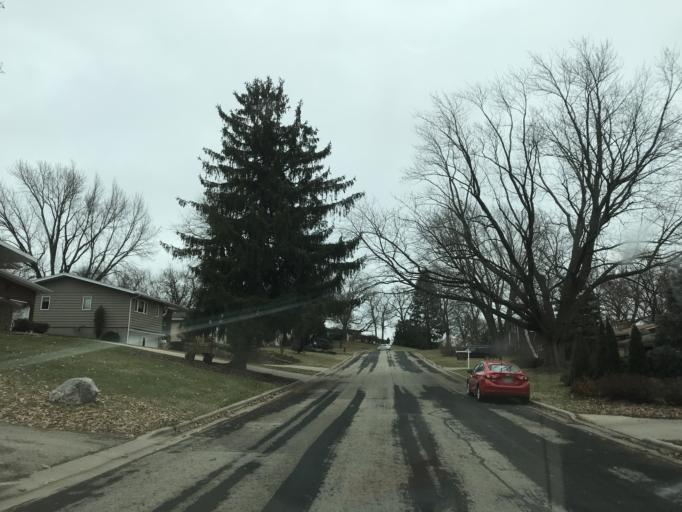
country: US
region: Wisconsin
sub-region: Dane County
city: Monona
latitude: 43.0532
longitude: -89.3268
